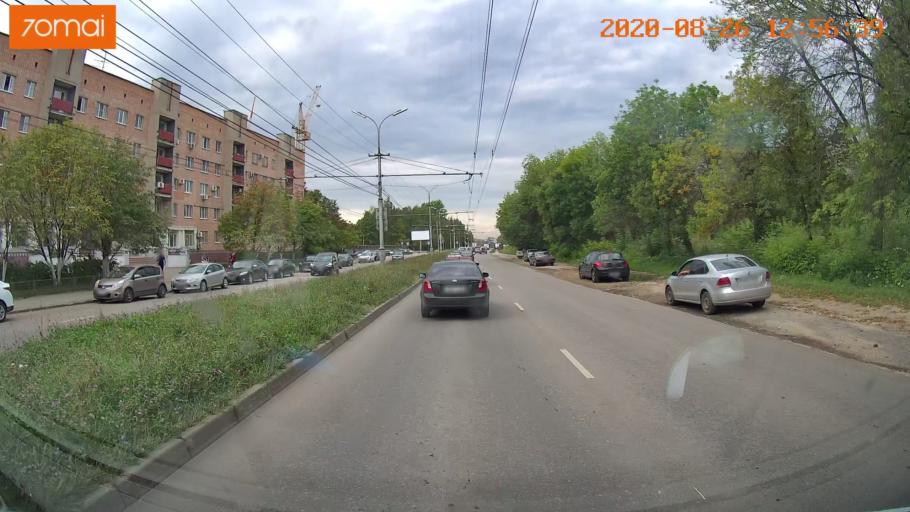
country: RU
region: Rjazan
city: Ryazan'
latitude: 54.6142
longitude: 39.7470
